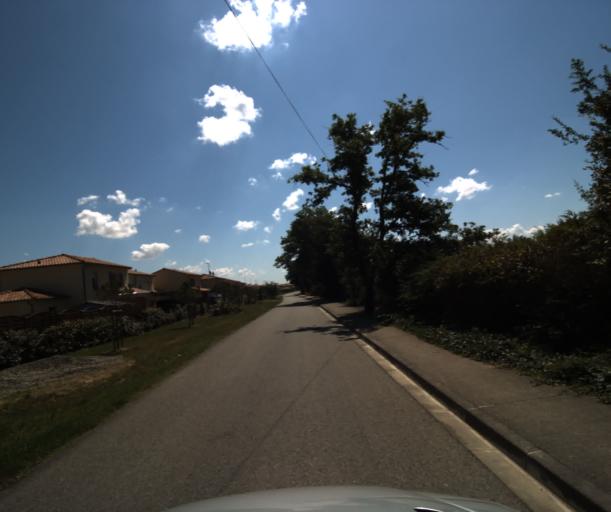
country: FR
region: Midi-Pyrenees
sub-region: Departement de la Haute-Garonne
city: Eaunes
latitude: 43.4228
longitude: 1.3494
